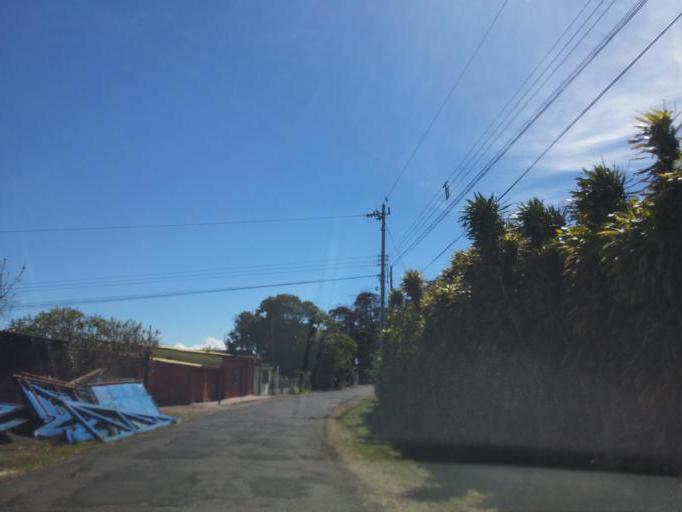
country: CR
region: Alajuela
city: Sabanilla
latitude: 10.1033
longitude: -84.1847
